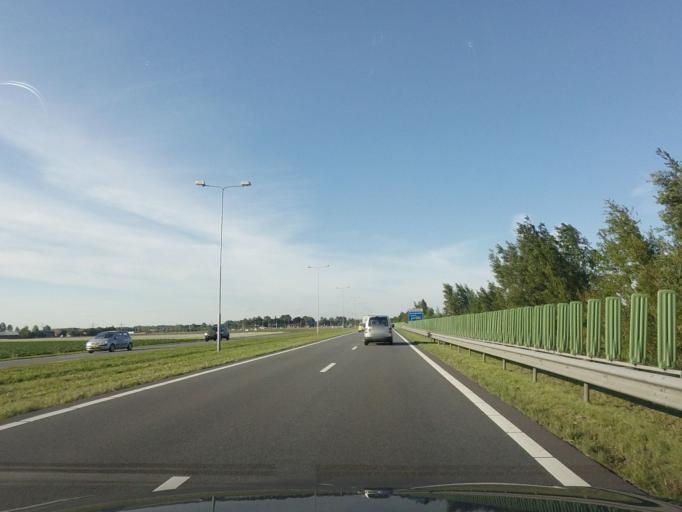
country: NL
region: North Holland
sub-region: Gemeente Haarlemmermeer
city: Hoofddorp
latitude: 52.3613
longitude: 4.7085
